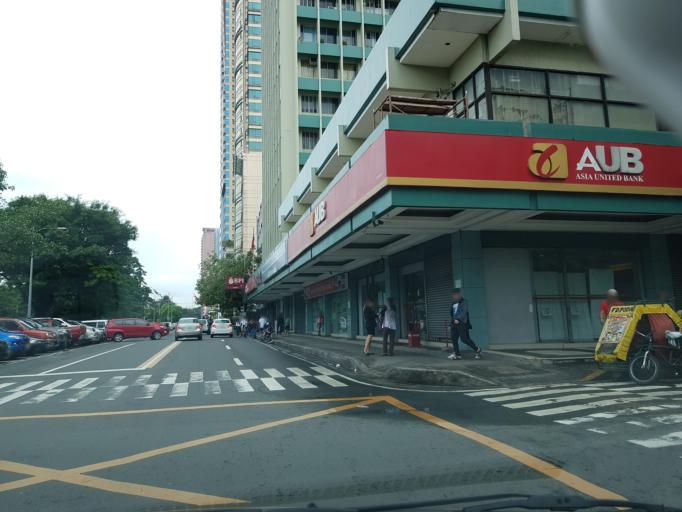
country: PH
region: Metro Manila
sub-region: City of Manila
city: Port Area
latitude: 14.5750
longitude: 120.9804
